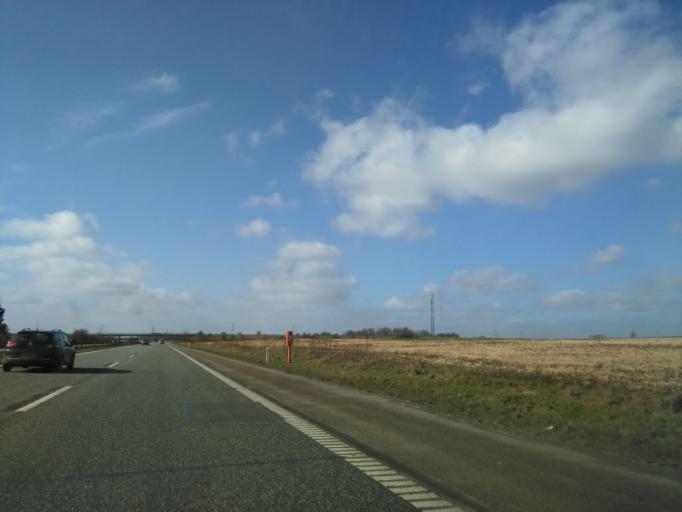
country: DK
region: Zealand
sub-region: Koge Kommune
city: Ejby
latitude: 55.4797
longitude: 12.1199
